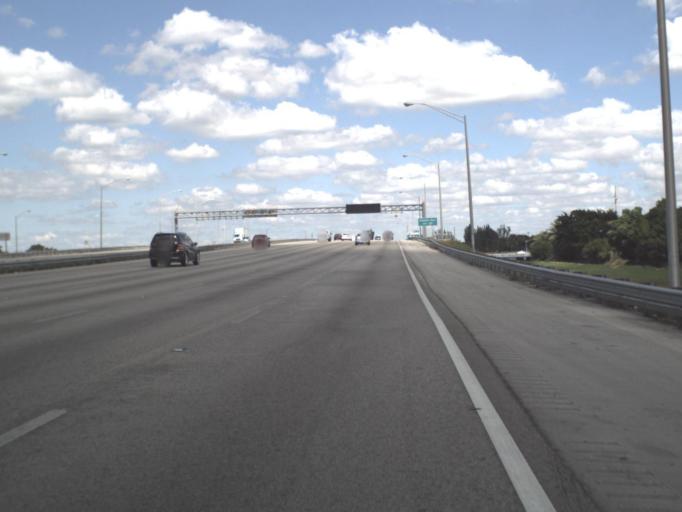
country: US
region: Florida
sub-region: Miami-Dade County
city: Sweetwater
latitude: 25.7650
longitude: -80.3853
